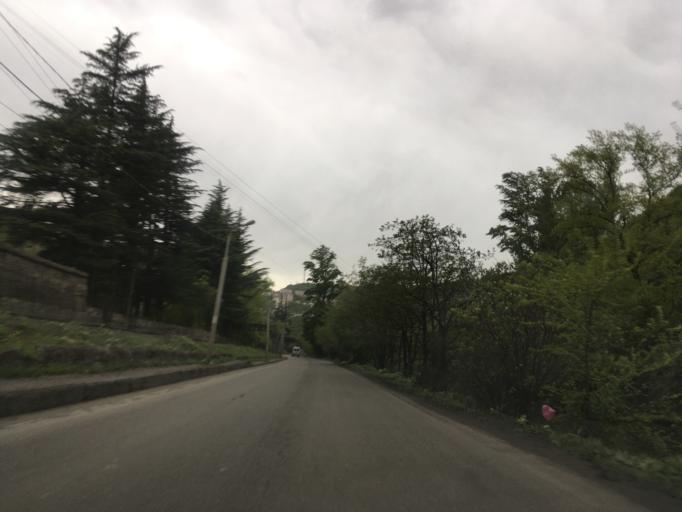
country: GE
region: Racha-Lechkhumi and Kvemo Svaneti
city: Gori
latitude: 42.2906
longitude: 43.2945
